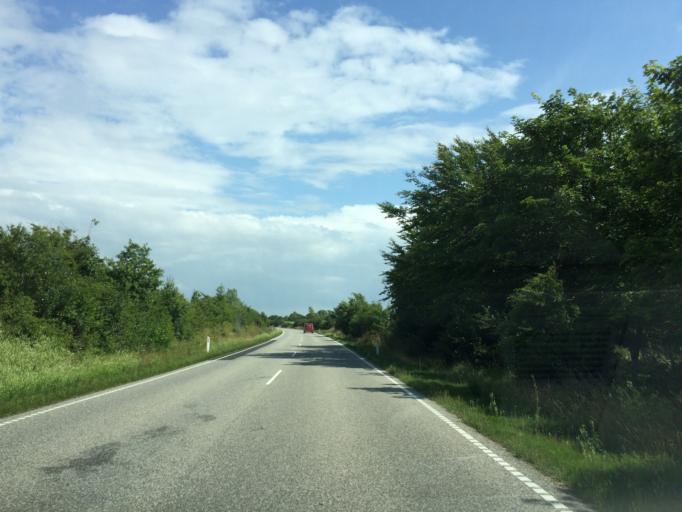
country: DK
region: Zealand
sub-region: Odsherred Kommune
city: Asnaes
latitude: 55.9638
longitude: 11.3648
